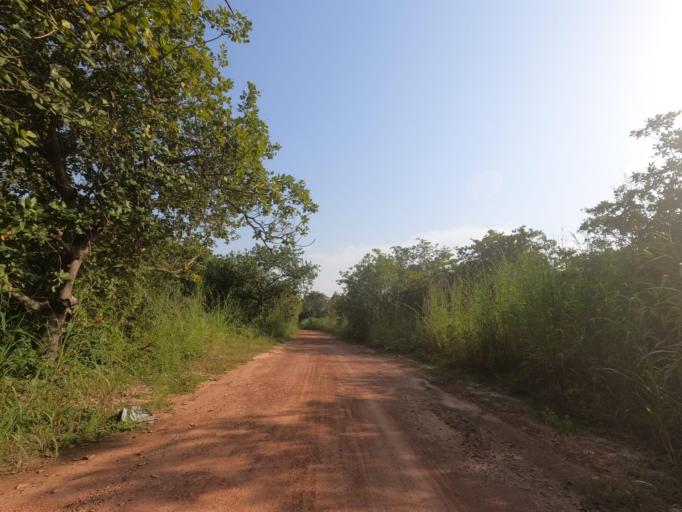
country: SN
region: Sedhiou
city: Sedhiou
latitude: 12.4142
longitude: -15.7315
